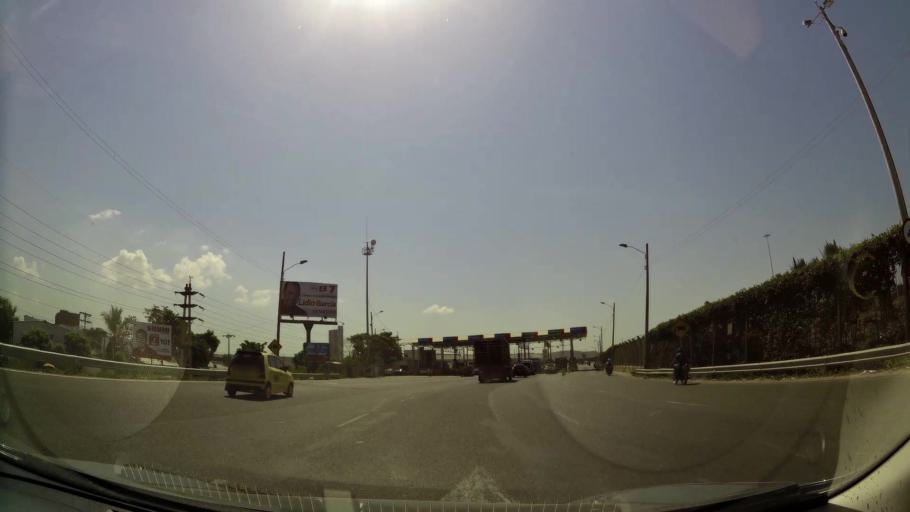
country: CO
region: Bolivar
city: Cartagena
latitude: 10.3838
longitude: -75.5061
